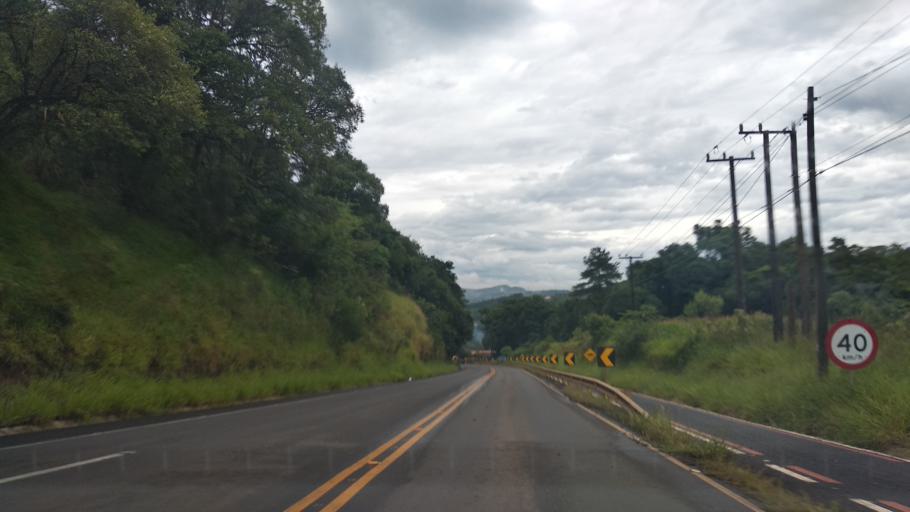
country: BR
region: Santa Catarina
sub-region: Videira
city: Videira
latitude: -27.0892
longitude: -51.2427
